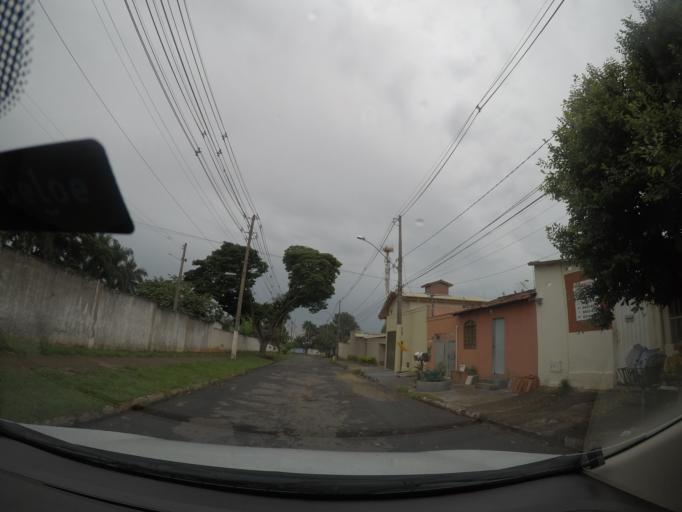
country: BR
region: Goias
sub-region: Goiania
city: Goiania
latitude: -16.6848
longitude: -49.2372
